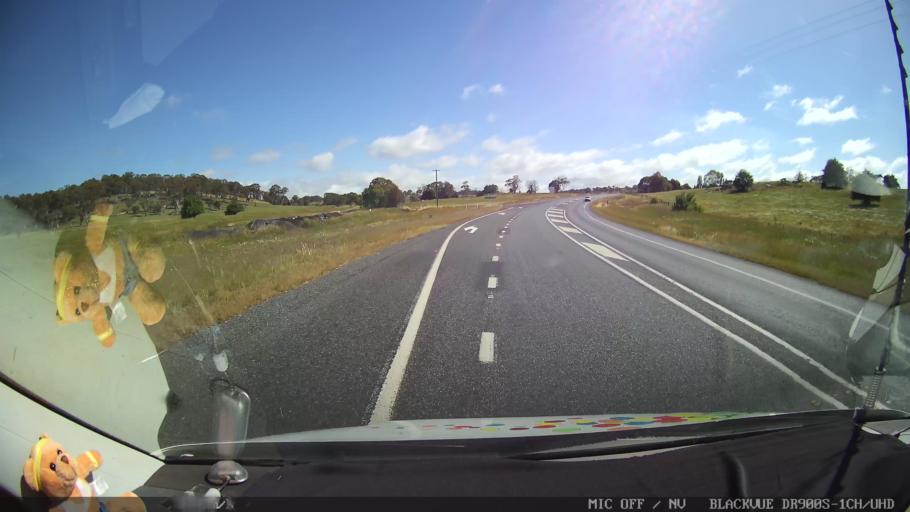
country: AU
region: New South Wales
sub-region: Guyra
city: Guyra
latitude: -30.1238
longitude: 151.6858
